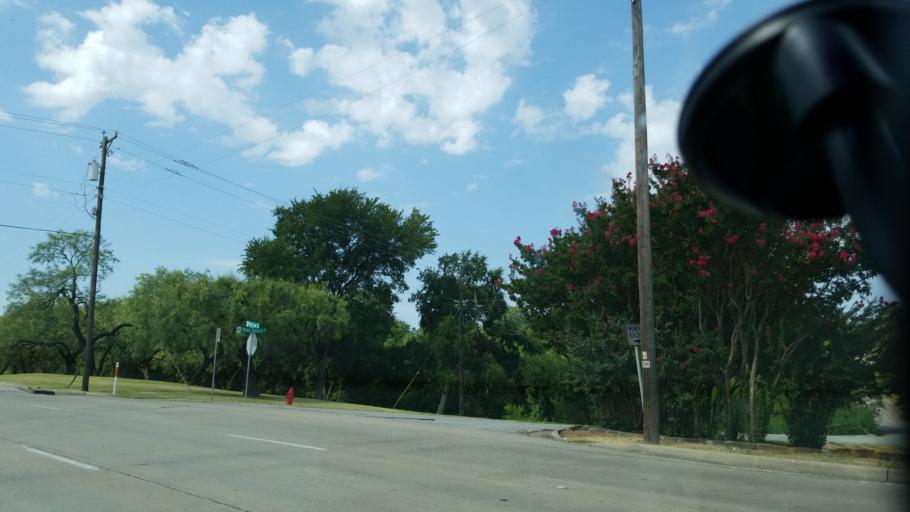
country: US
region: Texas
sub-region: Dallas County
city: Grand Prairie
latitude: 32.7517
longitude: -96.9947
